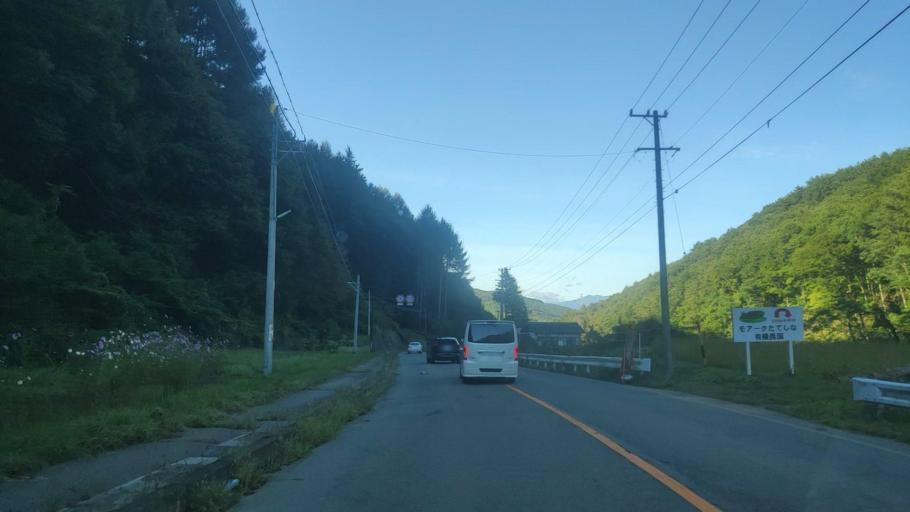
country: JP
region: Nagano
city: Kamimaruko
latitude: 36.2268
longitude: 138.2979
